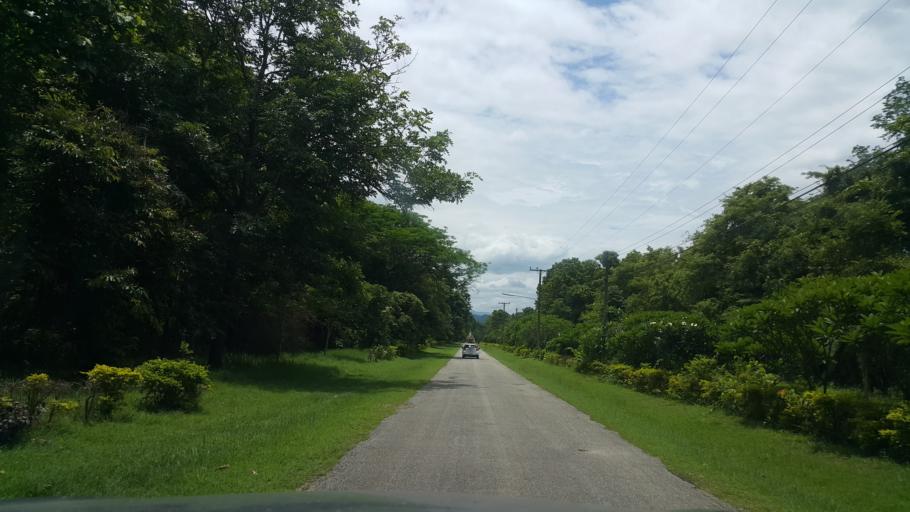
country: TH
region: Chiang Mai
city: Mae Taeng
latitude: 19.1827
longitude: 98.9621
